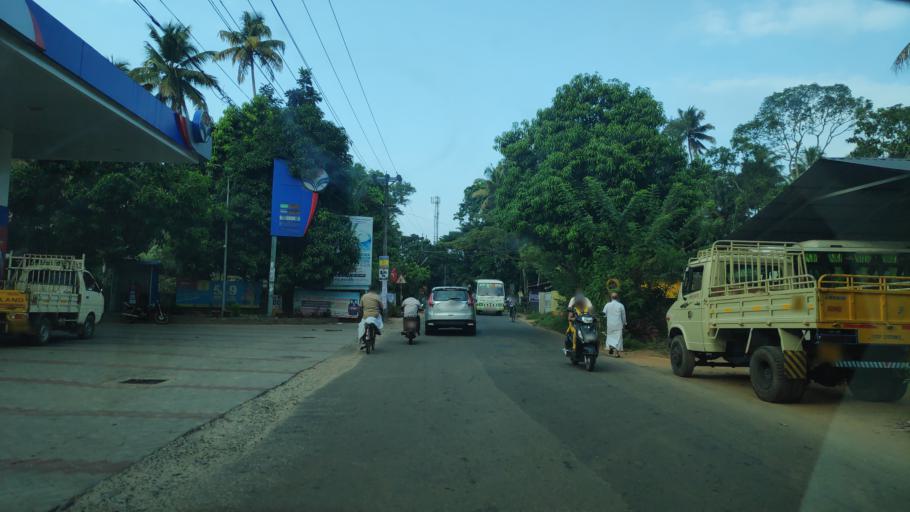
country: IN
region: Kerala
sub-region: Alappuzha
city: Alleppey
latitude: 9.5688
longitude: 76.3479
